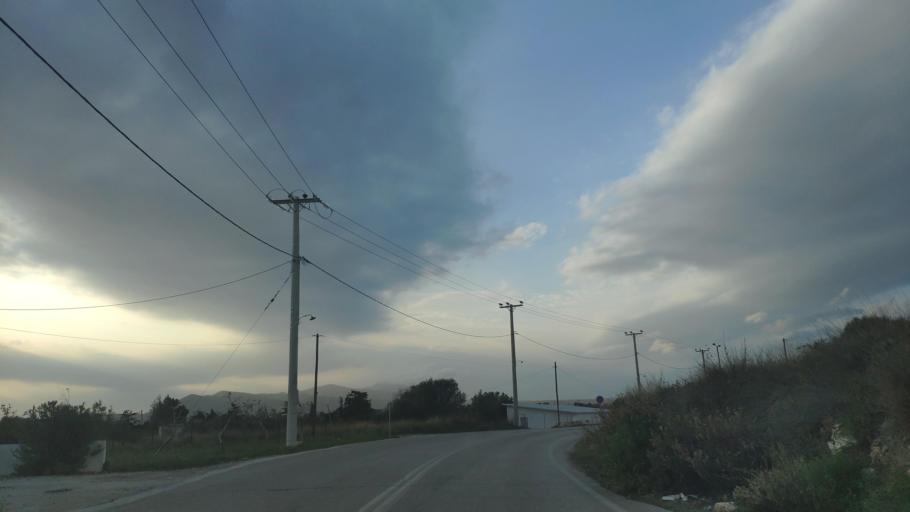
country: GR
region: Attica
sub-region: Nomarchia Dytikis Attikis
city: Nea Peramos
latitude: 37.9959
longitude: 23.3913
